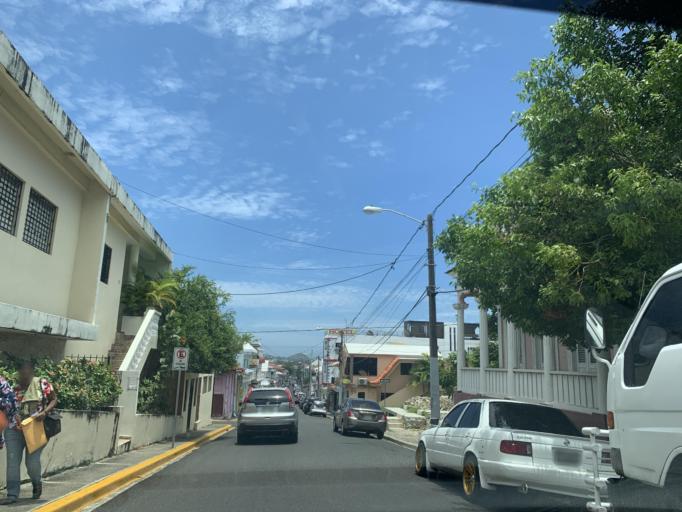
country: DO
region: Puerto Plata
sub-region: Puerto Plata
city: Puerto Plata
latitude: 19.7973
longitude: -70.6899
